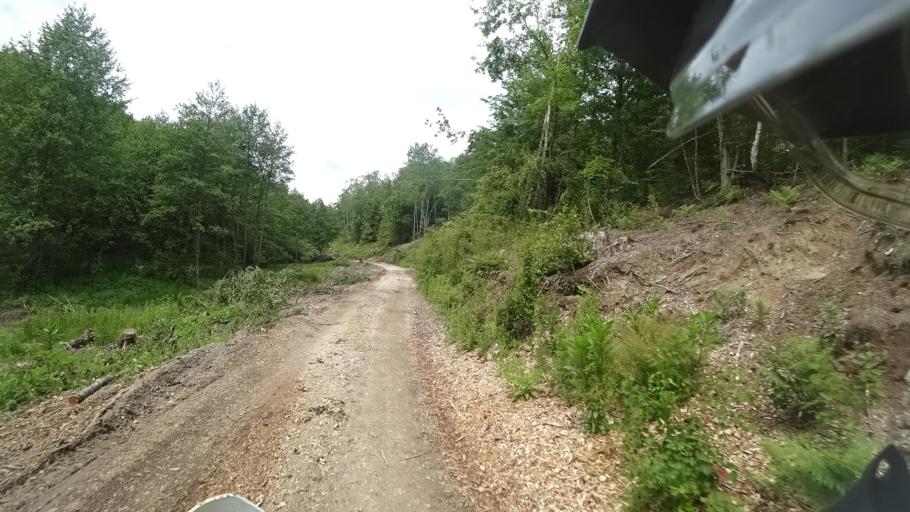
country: HR
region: Karlovacka
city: Vojnic
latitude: 45.2460
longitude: 15.6806
